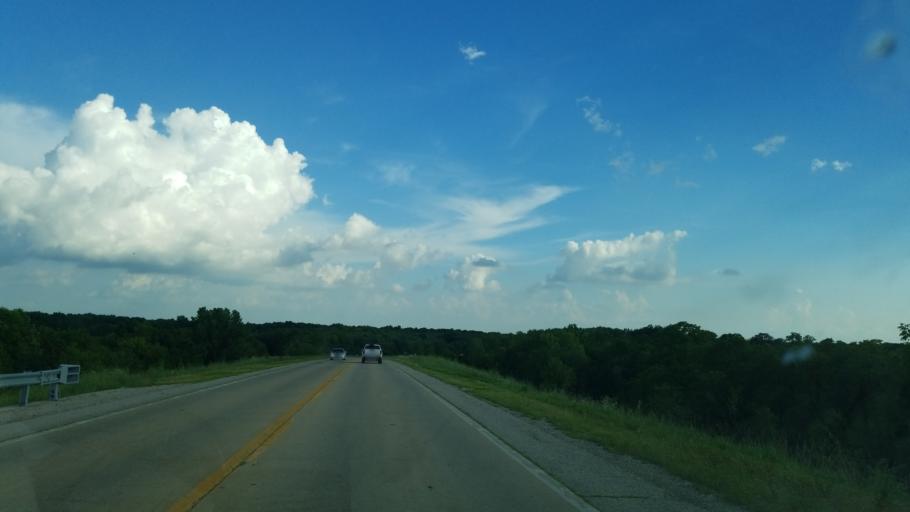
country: US
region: Illinois
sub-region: Marion County
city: Central City
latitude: 38.5798
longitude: -89.1084
